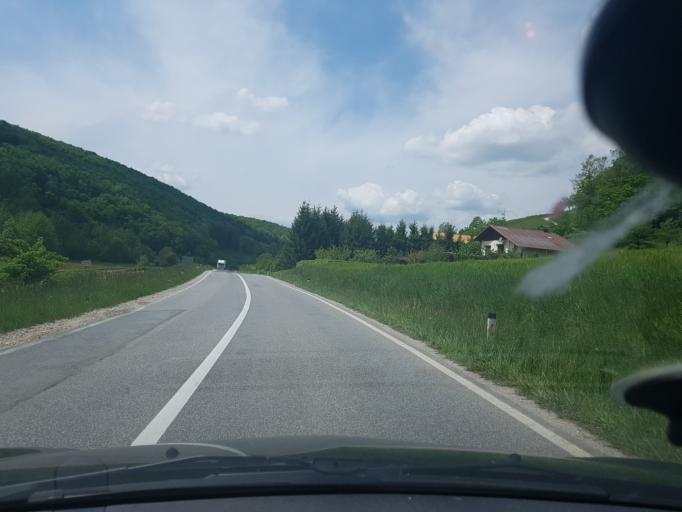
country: SI
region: Rogaska Slatina
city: Rogaska Slatina
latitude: 46.2398
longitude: 15.5975
